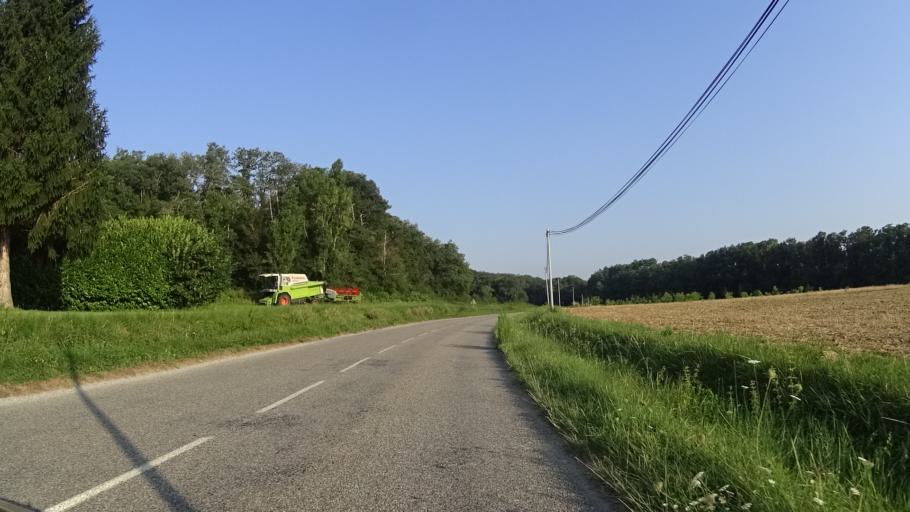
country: FR
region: Midi-Pyrenees
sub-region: Departement de l'Ariege
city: Mirepoix
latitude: 43.0748
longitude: 1.9404
